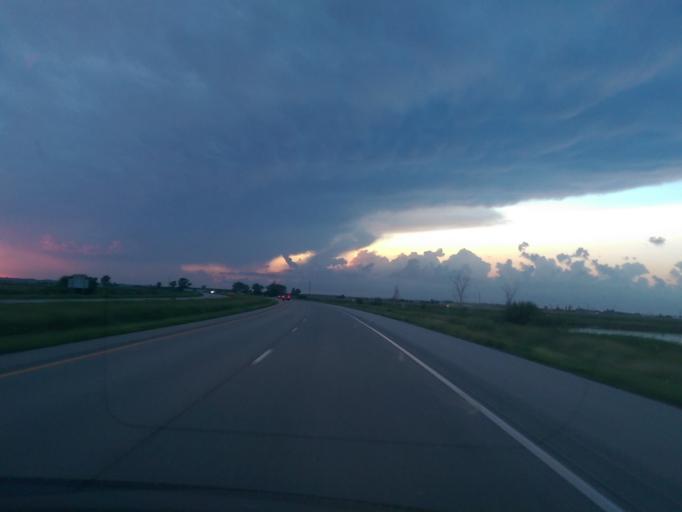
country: US
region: Nebraska
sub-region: Otoe County
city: Nebraska City
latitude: 40.7157
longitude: -95.8021
